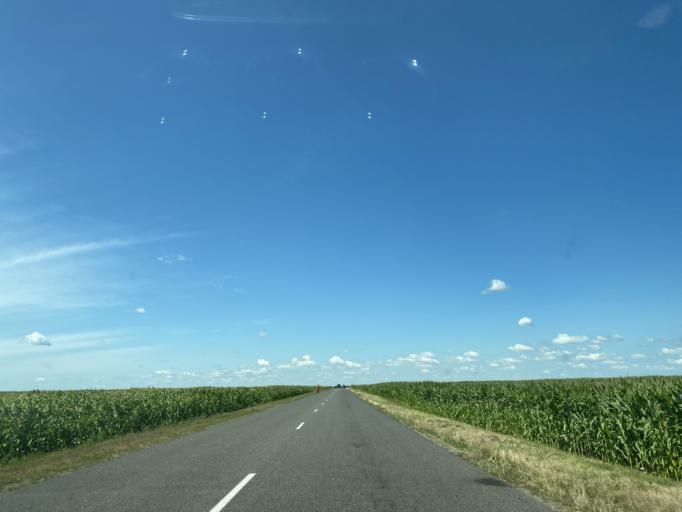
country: BY
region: Brest
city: Ivanava
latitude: 52.1757
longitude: 25.5843
